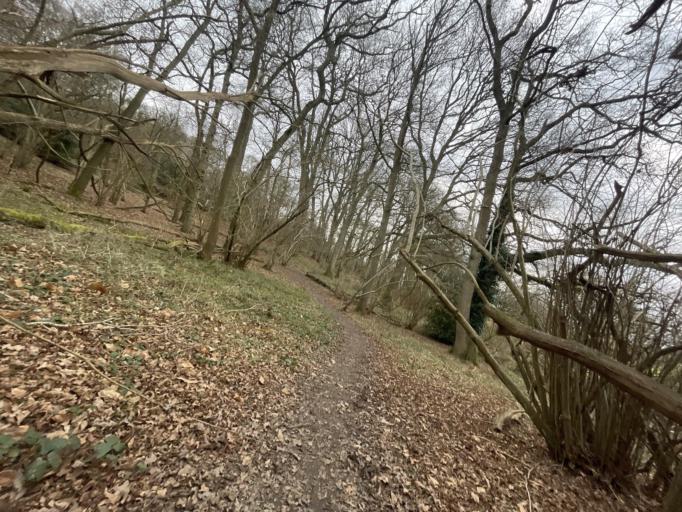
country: GB
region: England
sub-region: West Berkshire
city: Theale
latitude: 51.4497
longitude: -1.0655
